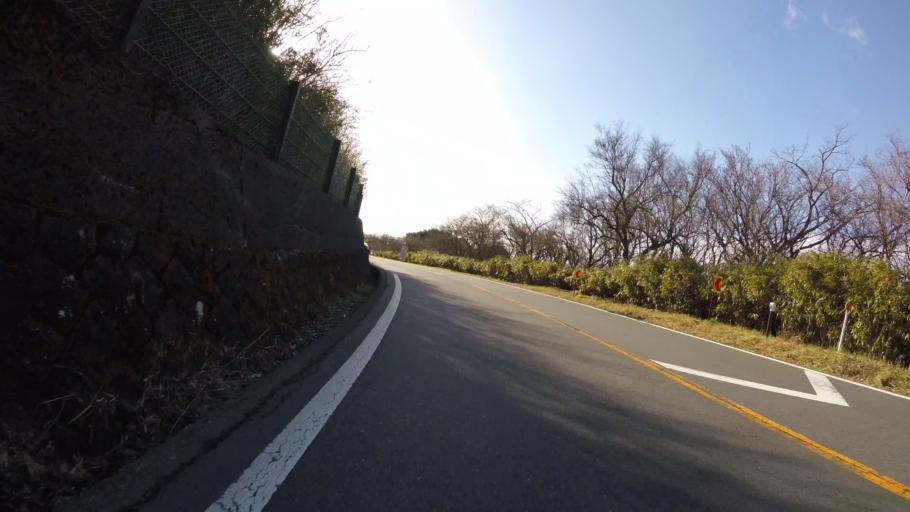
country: JP
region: Kanagawa
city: Hakone
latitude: 35.1622
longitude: 139.0244
